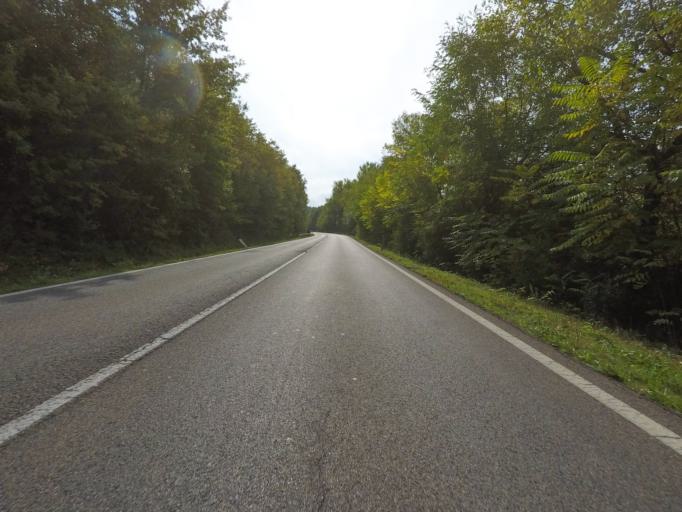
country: IT
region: Tuscany
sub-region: Provincia di Siena
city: Rosia
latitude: 43.1956
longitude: 11.2766
